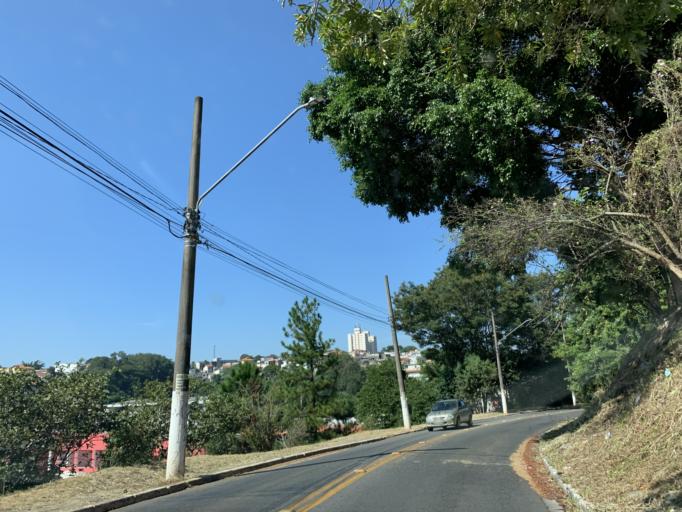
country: BR
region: Sao Paulo
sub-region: Caieiras
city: Caieiras
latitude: -23.4473
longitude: -46.7480
